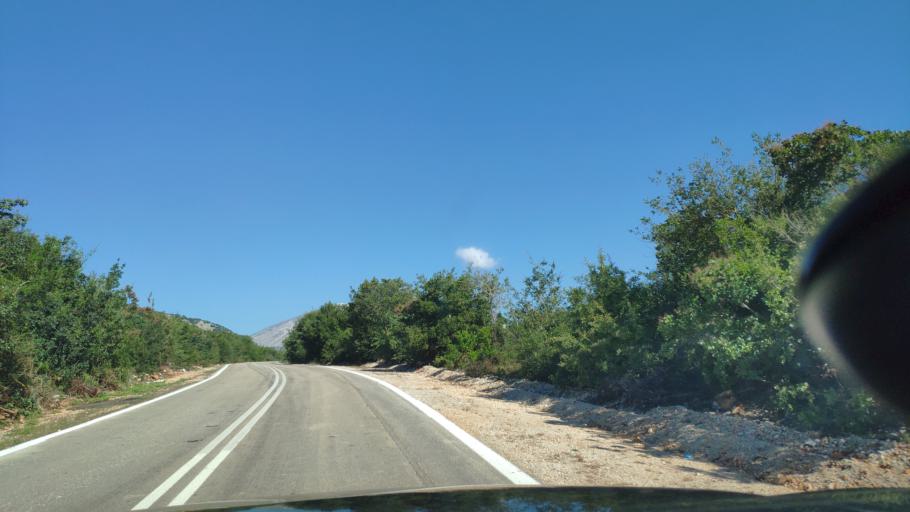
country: GR
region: West Greece
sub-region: Nomos Aitolias kai Akarnanias
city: Fitiai
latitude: 38.6824
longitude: 21.1273
